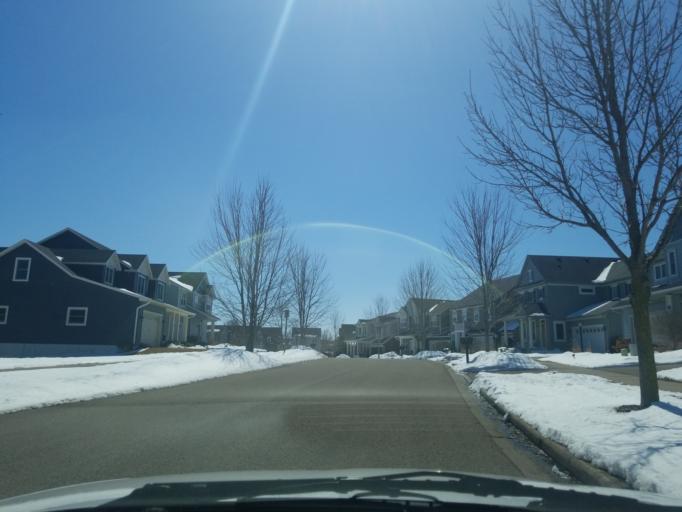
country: US
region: Wisconsin
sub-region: Saint Croix County
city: Hudson
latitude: 44.9555
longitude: -92.7001
